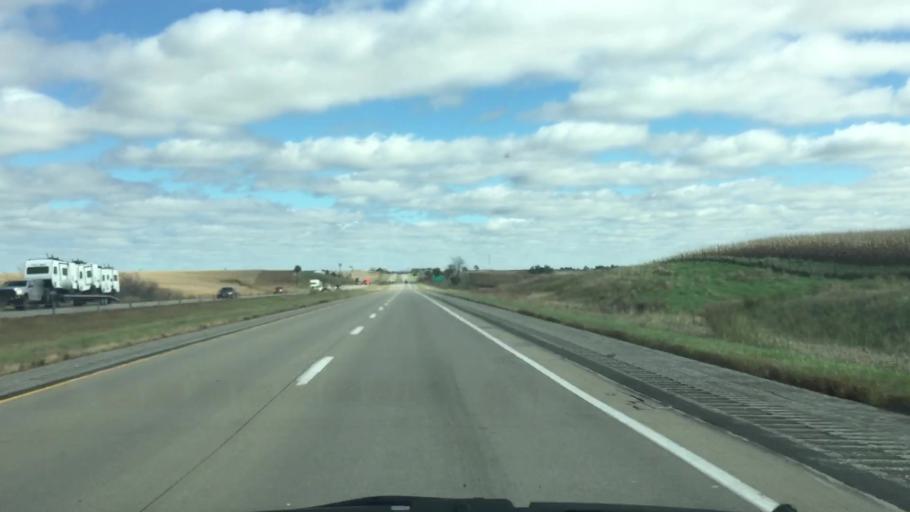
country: US
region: Iowa
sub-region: Iowa County
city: Williamsburg
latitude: 41.6916
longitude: -92.0988
